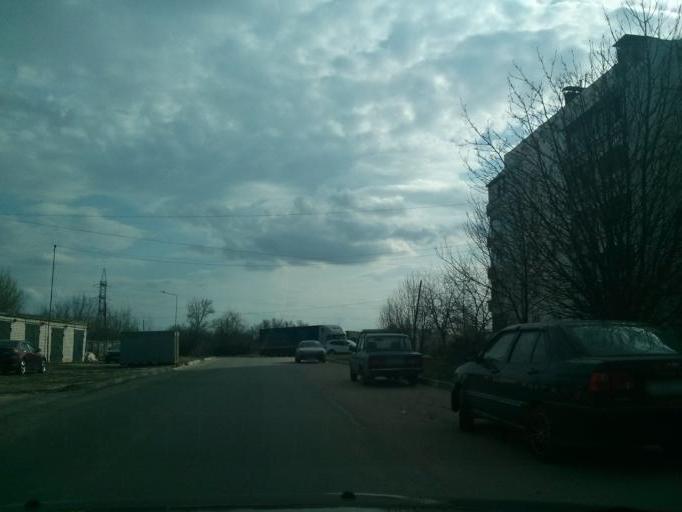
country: RU
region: Nizjnij Novgorod
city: Nizhniy Novgorod
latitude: 56.2614
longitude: 44.0091
